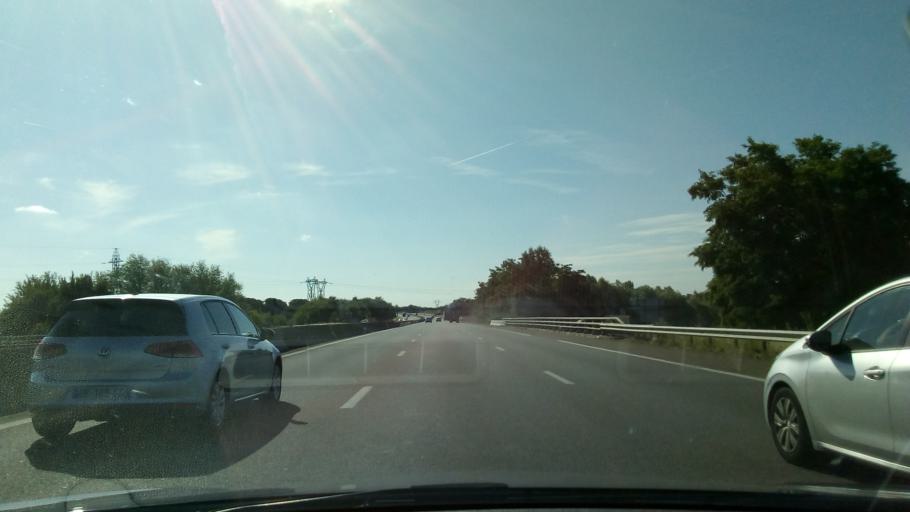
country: FR
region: Ile-de-France
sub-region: Departement de Seine-et-Marne
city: Moissy-Cramayel
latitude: 48.6080
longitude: 2.5803
